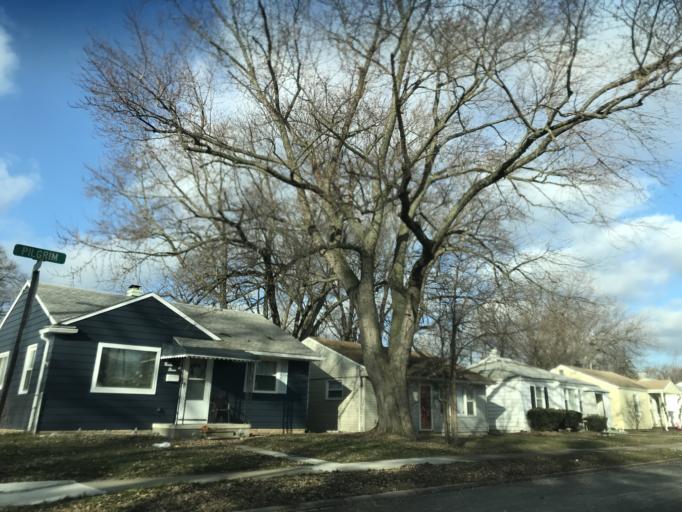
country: US
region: Michigan
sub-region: Oakland County
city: Hazel Park
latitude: 42.4633
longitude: -83.1110
